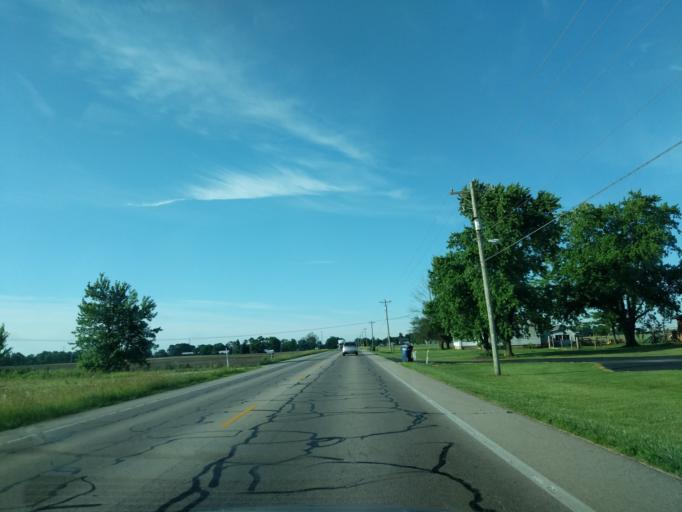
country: US
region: Indiana
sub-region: Madison County
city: Ingalls
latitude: 39.8766
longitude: -85.7704
